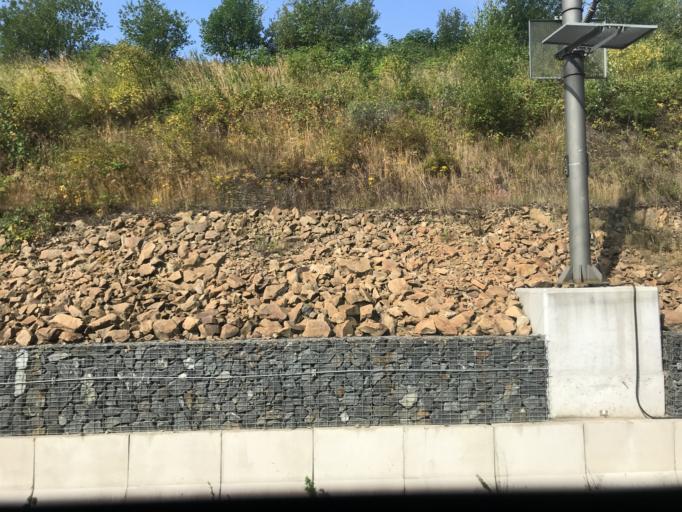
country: CZ
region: Central Bohemia
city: Votice
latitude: 49.6558
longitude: 14.6239
